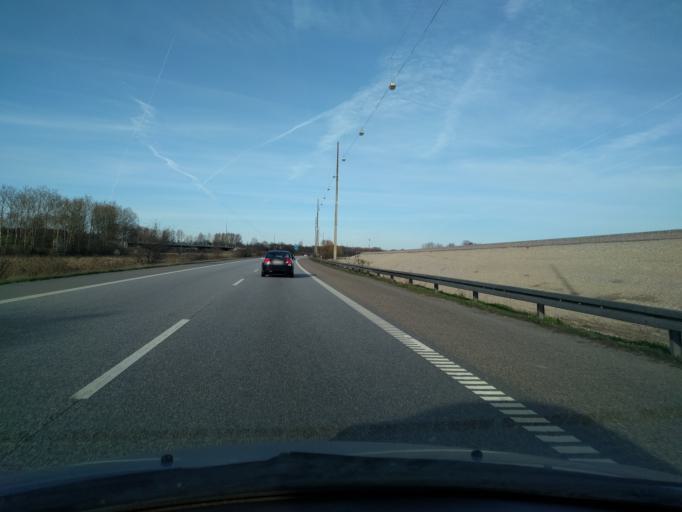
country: DK
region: Capital Region
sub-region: Ishoj Kommune
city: Ishoj
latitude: 55.6379
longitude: 12.3408
